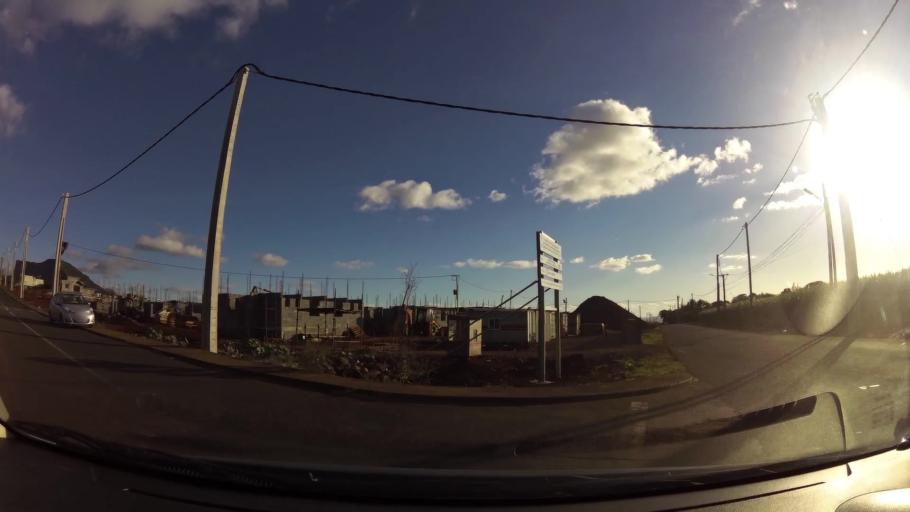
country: MU
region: Black River
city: Petite Riviere
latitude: -20.2146
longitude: 57.4621
